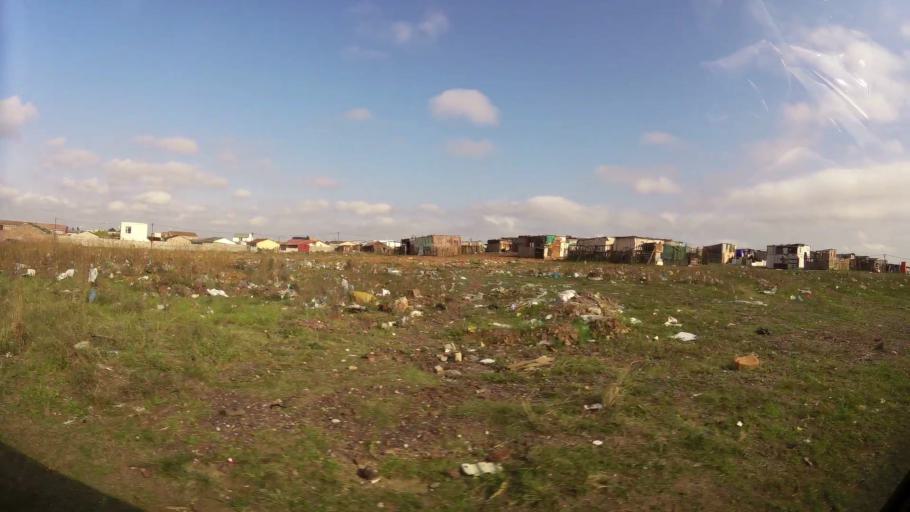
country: ZA
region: Eastern Cape
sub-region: Nelson Mandela Bay Metropolitan Municipality
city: Port Elizabeth
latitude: -33.9171
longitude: 25.5383
